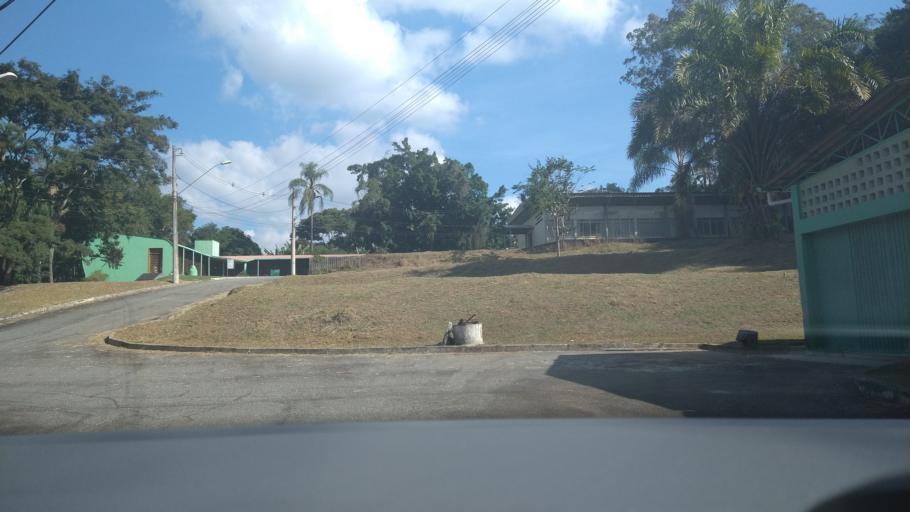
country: BR
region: Minas Gerais
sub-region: Vicosa
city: Vicosa
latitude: -20.7700
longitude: -42.8754
